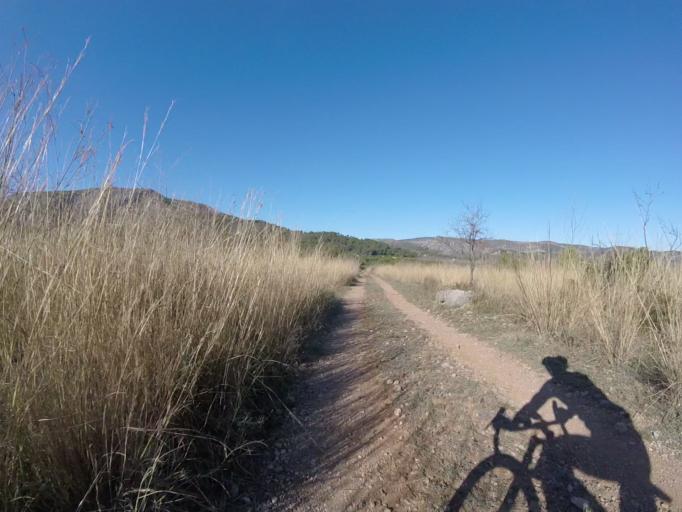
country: ES
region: Valencia
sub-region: Provincia de Castello
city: Orpesa/Oropesa del Mar
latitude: 40.1227
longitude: 0.1136
